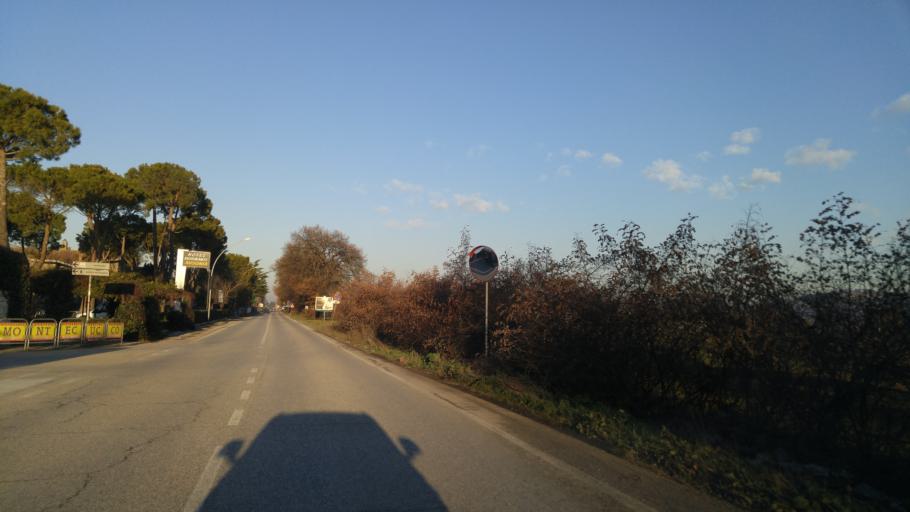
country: IT
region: The Marches
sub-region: Provincia di Pesaro e Urbino
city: Monte Porzio
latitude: 43.6884
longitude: 13.0477
